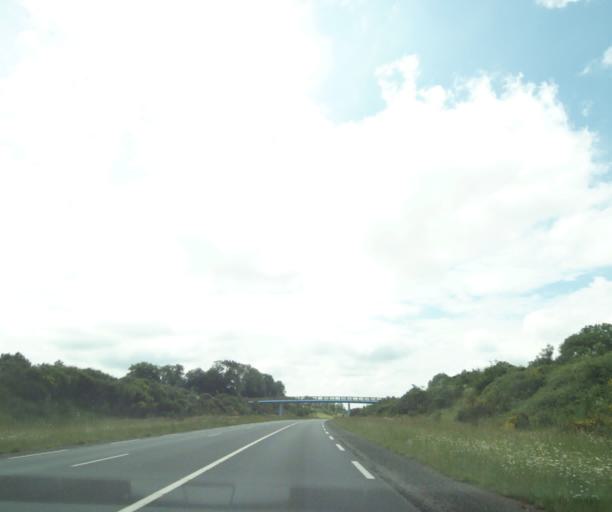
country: FR
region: Poitou-Charentes
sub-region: Departement des Deux-Sevres
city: Saint-Pardoux
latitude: 46.5342
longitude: -0.3157
